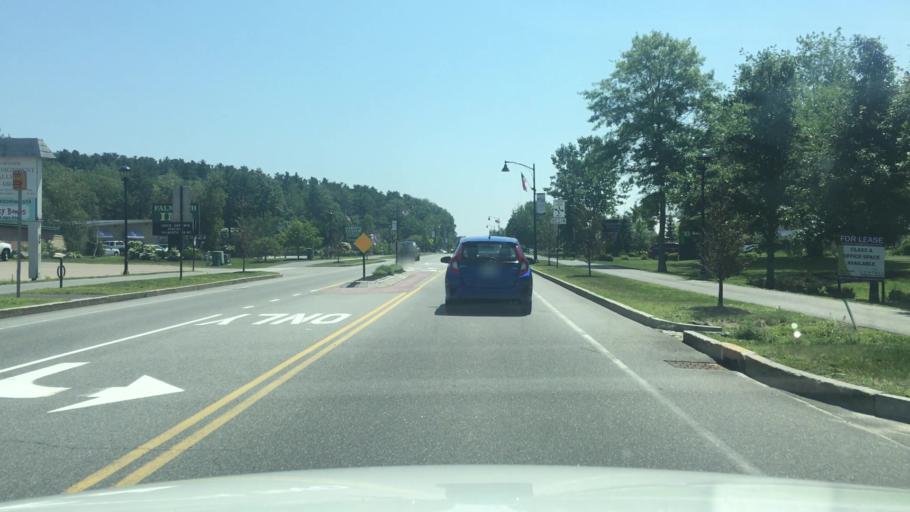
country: US
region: Maine
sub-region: Cumberland County
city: Falmouth
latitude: 43.7185
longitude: -70.2331
